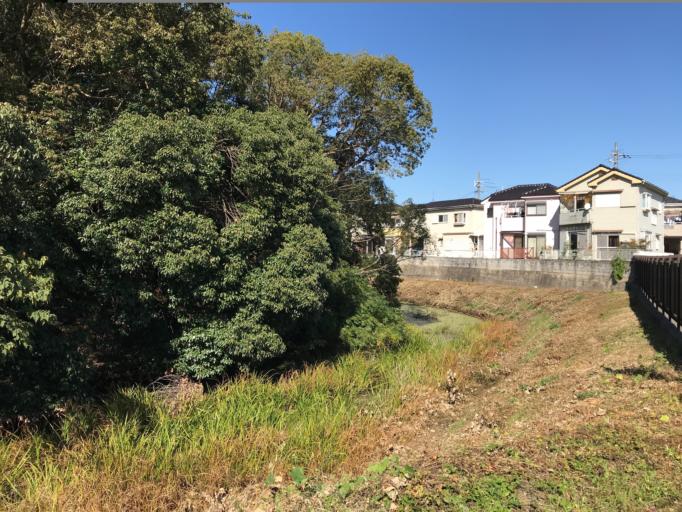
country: JP
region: Osaka
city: Kashihara
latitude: 34.5486
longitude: 135.6104
